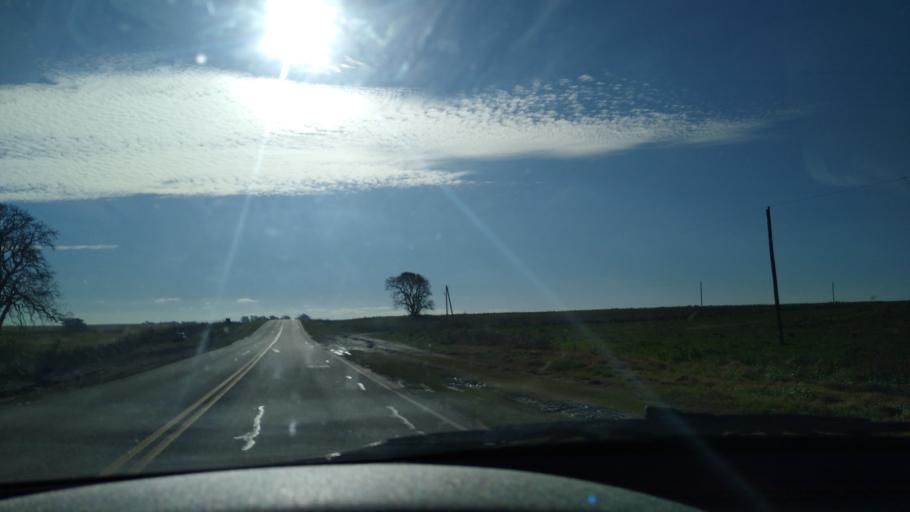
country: AR
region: Entre Rios
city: Aranguren
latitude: -32.3457
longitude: -60.3688
